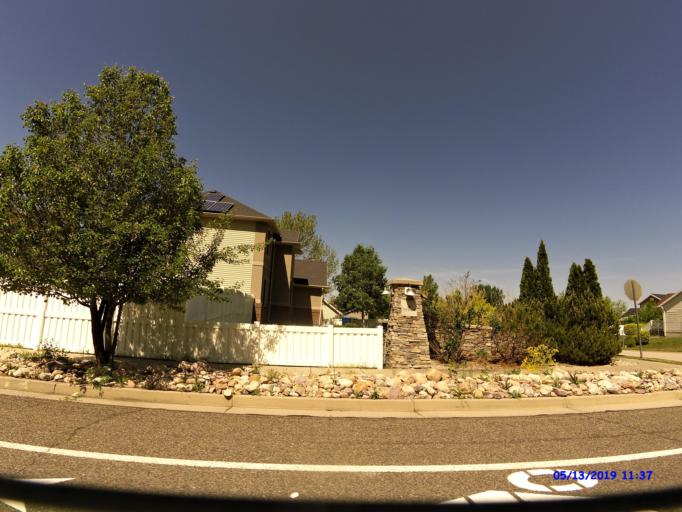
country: US
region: Utah
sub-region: Weber County
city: North Ogden
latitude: 41.2779
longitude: -111.9503
